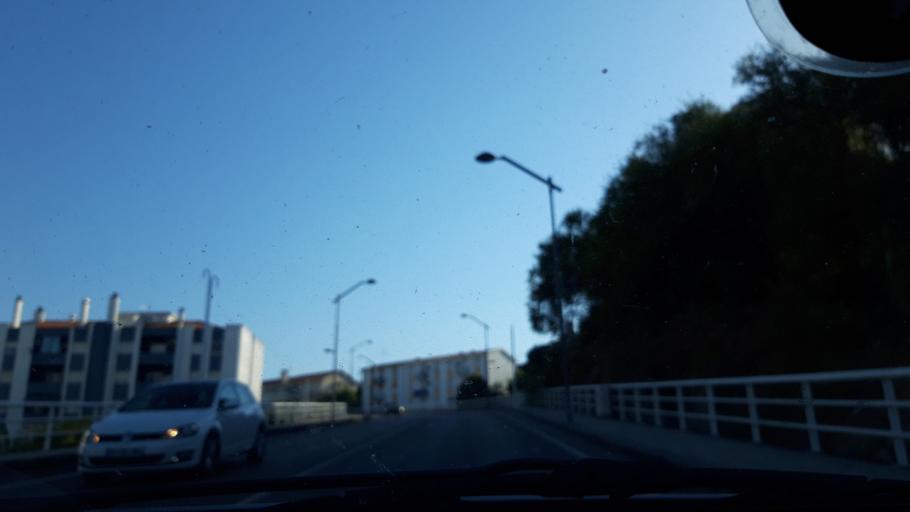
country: PT
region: Santarem
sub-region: Torres Novas
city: Torres Novas
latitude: 39.4797
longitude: -8.5452
